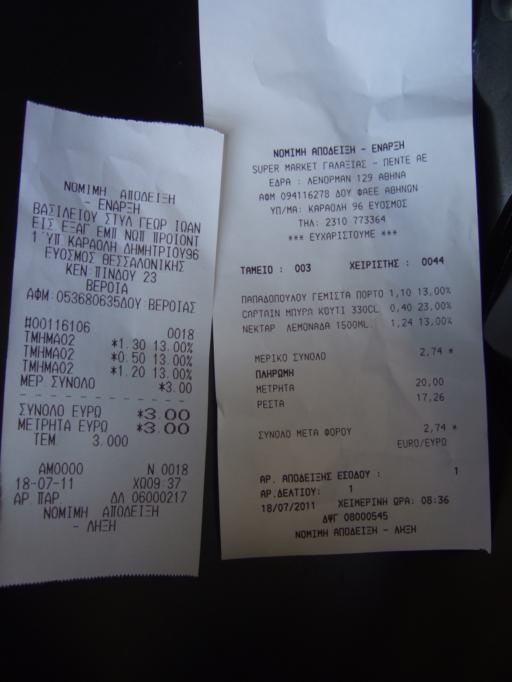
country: GR
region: Central Macedonia
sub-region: Nomos Thessalonikis
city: Evosmos
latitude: 40.6670
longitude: 22.9127
